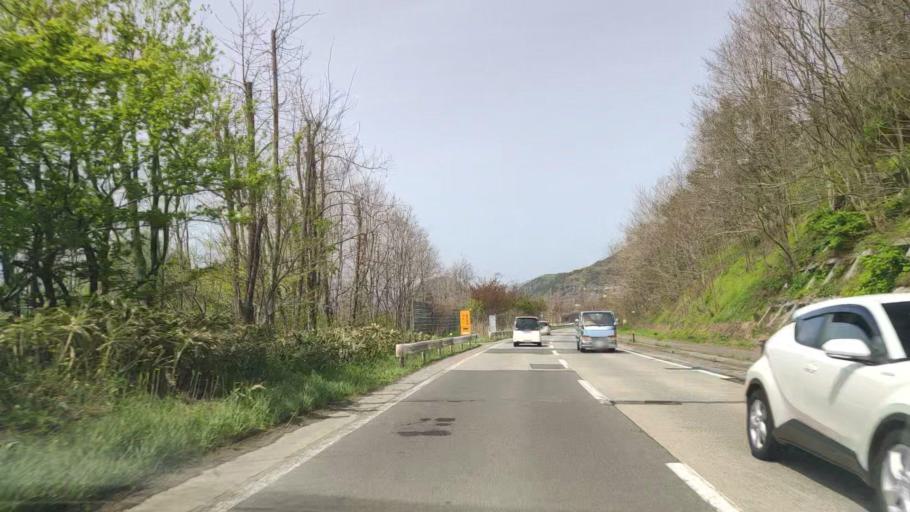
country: JP
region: Aomori
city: Aomori Shi
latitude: 40.8650
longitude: 140.8456
